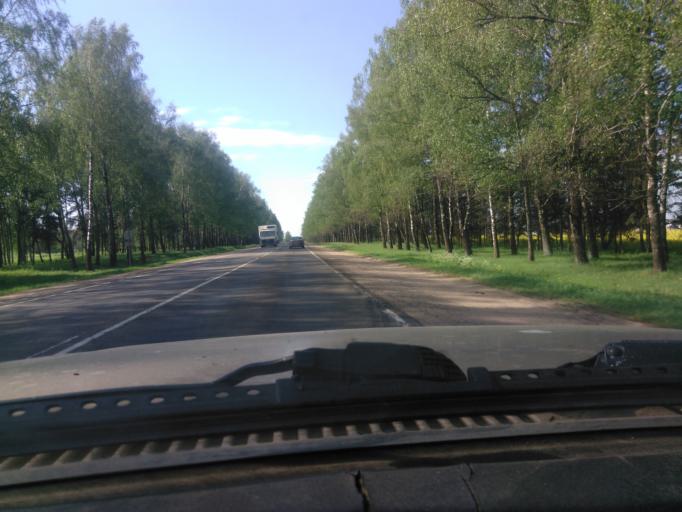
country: BY
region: Mogilev
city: Buynichy
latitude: 53.8462
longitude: 30.2510
